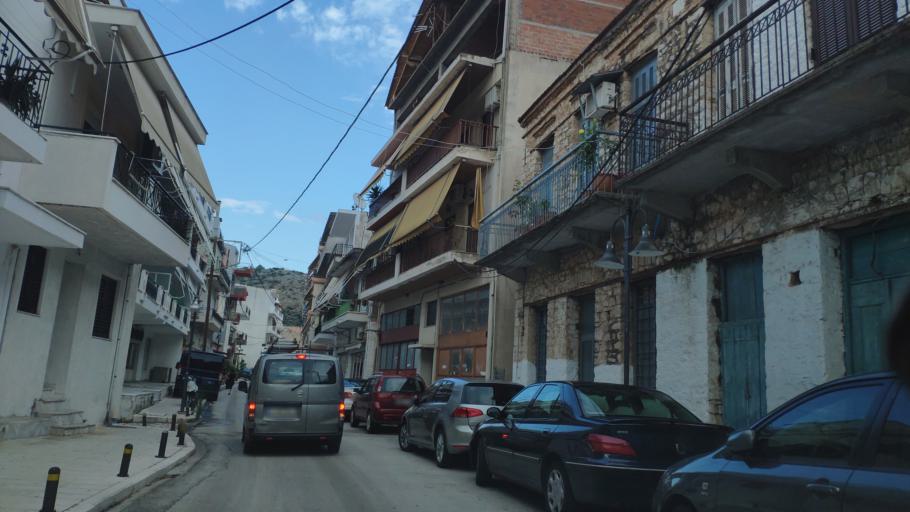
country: GR
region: West Greece
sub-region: Nomos Aitolias kai Akarnanias
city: Amfilochia
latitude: 38.8647
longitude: 21.1712
